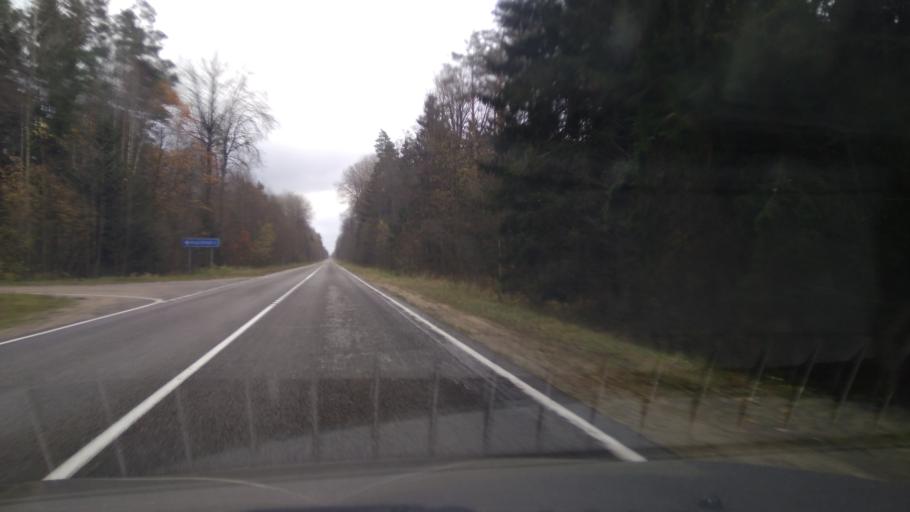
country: BY
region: Minsk
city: Urechcha
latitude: 53.2161
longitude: 27.8511
